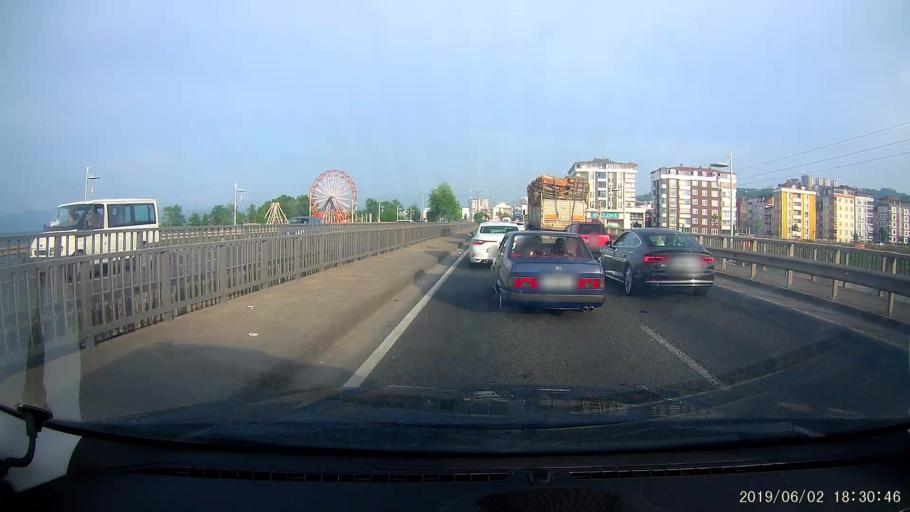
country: TR
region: Ordu
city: Fatsa
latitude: 41.0377
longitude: 37.4918
